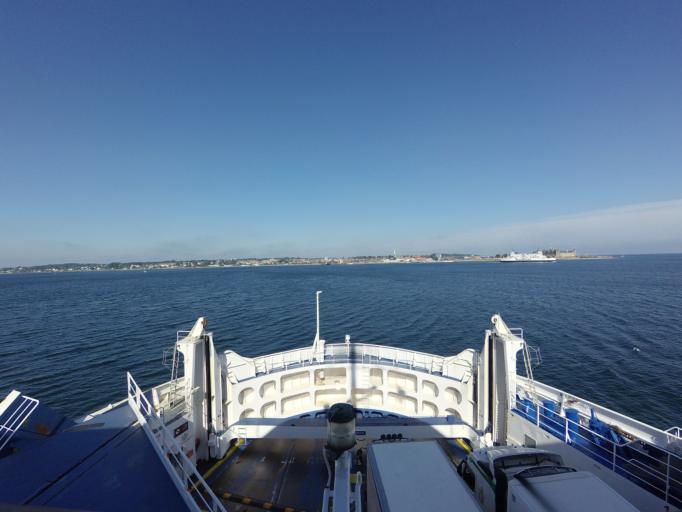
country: DK
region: Capital Region
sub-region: Helsingor Kommune
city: Helsingor
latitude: 56.0303
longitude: 12.6337
